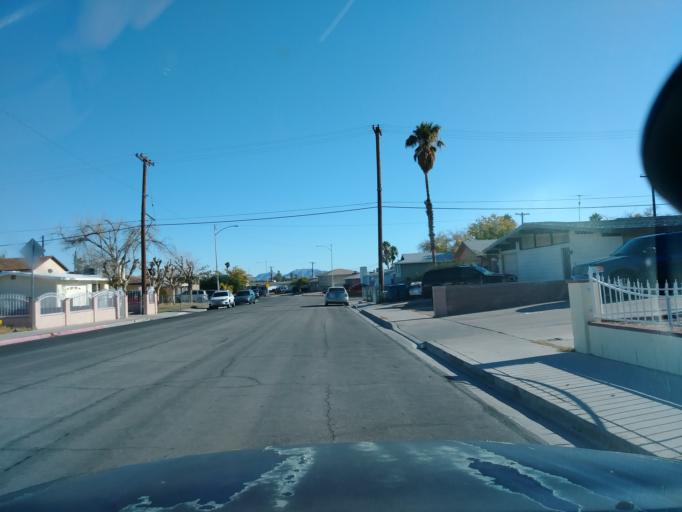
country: US
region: Nevada
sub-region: Clark County
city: Spring Valley
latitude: 36.1720
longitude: -115.2304
